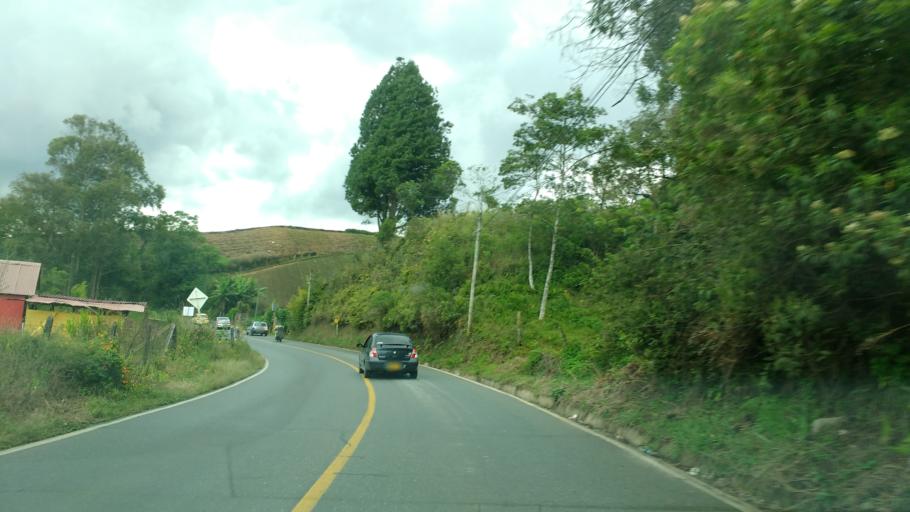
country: CO
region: Antioquia
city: Marinilla
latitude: 6.1929
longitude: -75.2893
